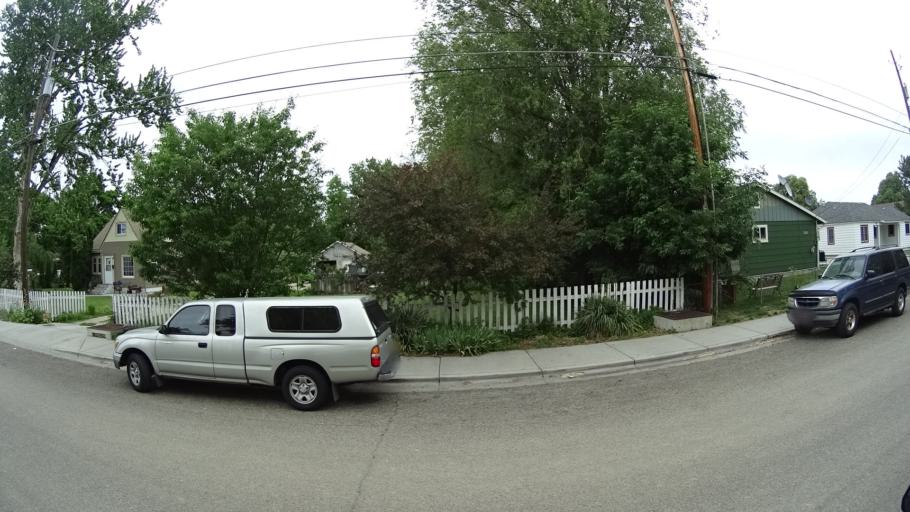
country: US
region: Idaho
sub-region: Ada County
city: Boise
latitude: 43.5810
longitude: -116.2206
